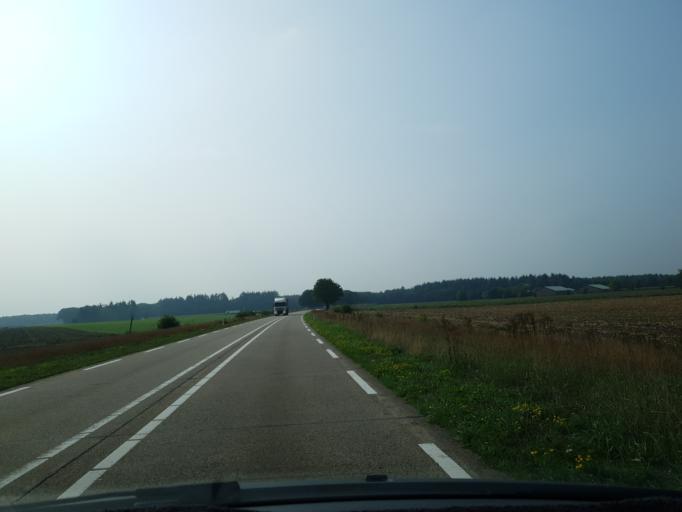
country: NL
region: North Brabant
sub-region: Bergeijk
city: Bergeyk
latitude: 51.3366
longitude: 5.3763
